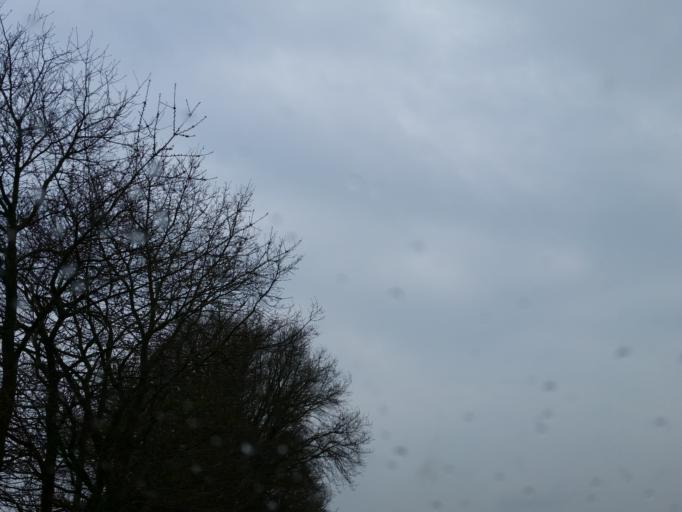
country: DE
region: Lower Saxony
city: Alfstedt
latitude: 53.5736
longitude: 9.0104
